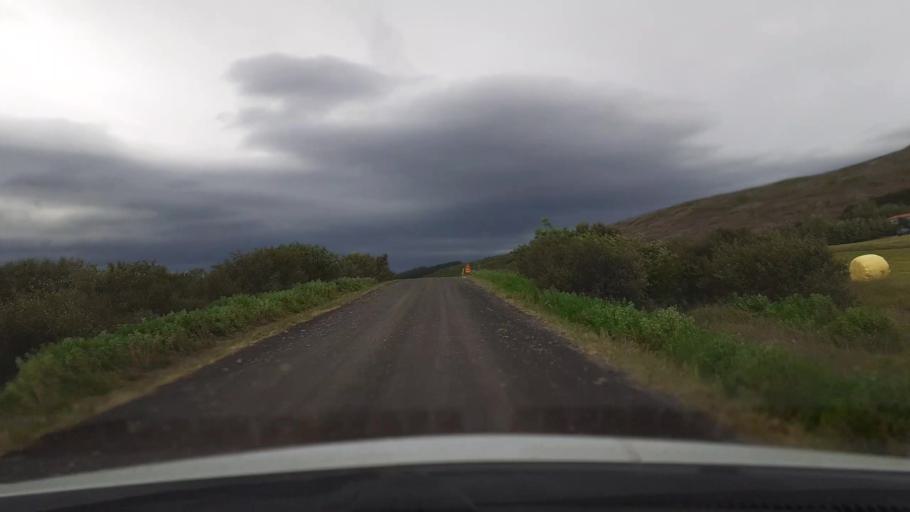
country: IS
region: Capital Region
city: Mosfellsbaer
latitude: 64.5261
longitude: -21.4830
